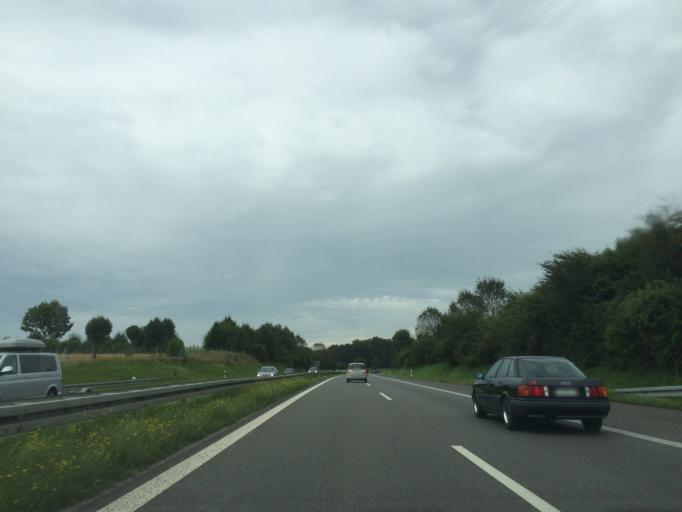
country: DE
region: Baden-Wuerttemberg
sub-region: Tuebingen Region
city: Baindt
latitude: 47.8588
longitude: 9.6474
